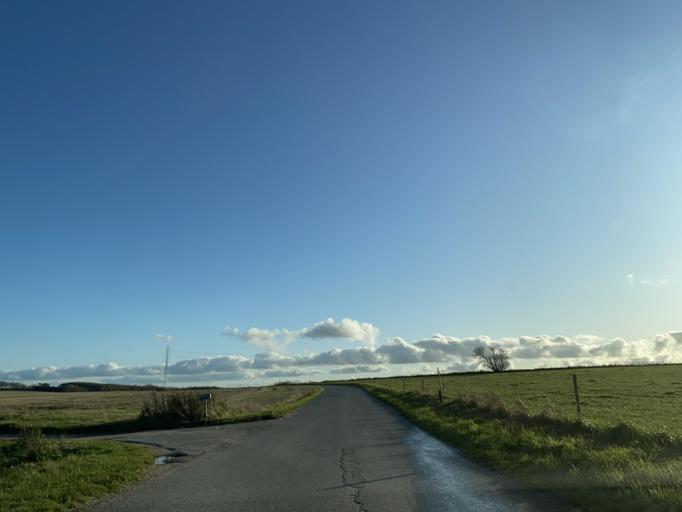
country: DK
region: Central Jutland
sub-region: Viborg Kommune
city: Bjerringbro
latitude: 56.3522
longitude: 9.7171
